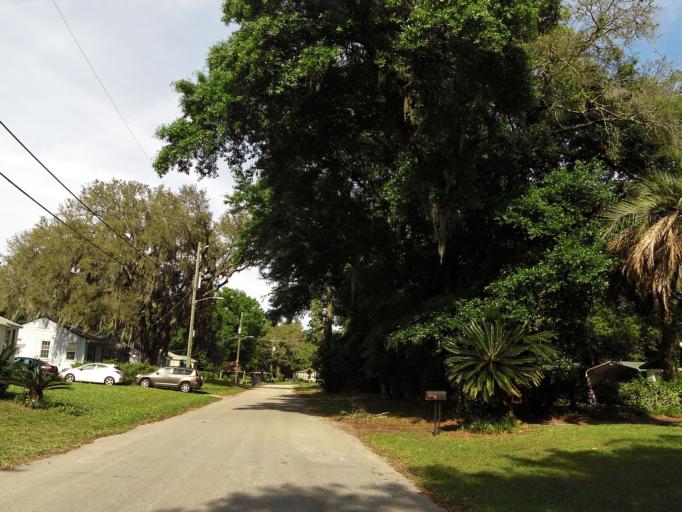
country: US
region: Florida
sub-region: Duval County
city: Jacksonville
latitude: 30.3155
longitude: -81.5961
